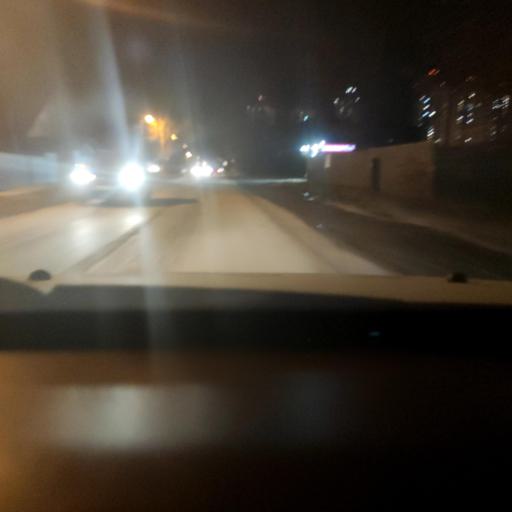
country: RU
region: Perm
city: Perm
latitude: 58.0113
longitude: 56.3202
